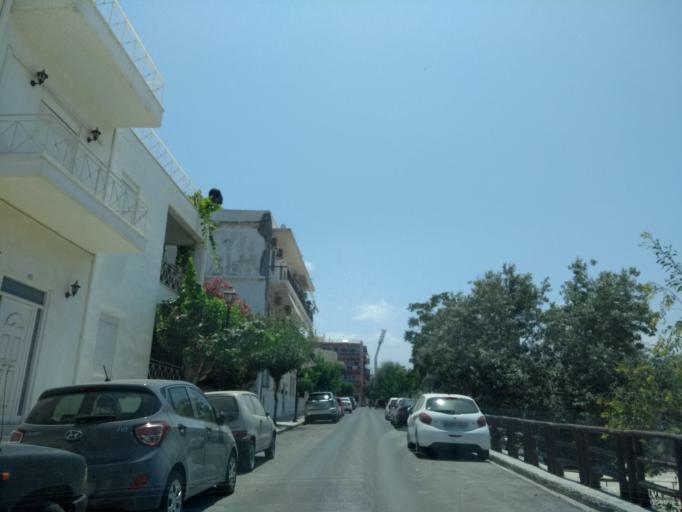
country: GR
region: Crete
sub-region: Nomos Chanias
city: Chania
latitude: 35.5168
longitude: 24.0246
